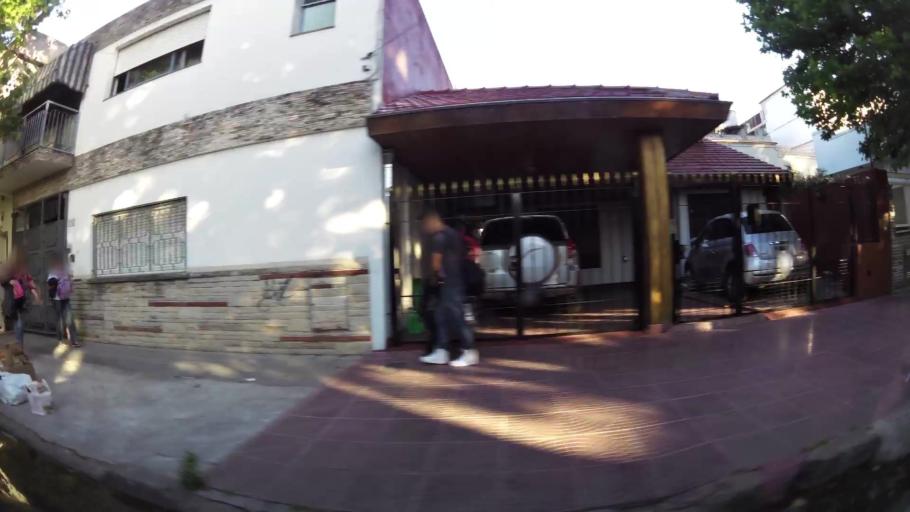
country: AR
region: Buenos Aires
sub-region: Partido de General San Martin
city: General San Martin
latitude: -34.5683
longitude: -58.5470
